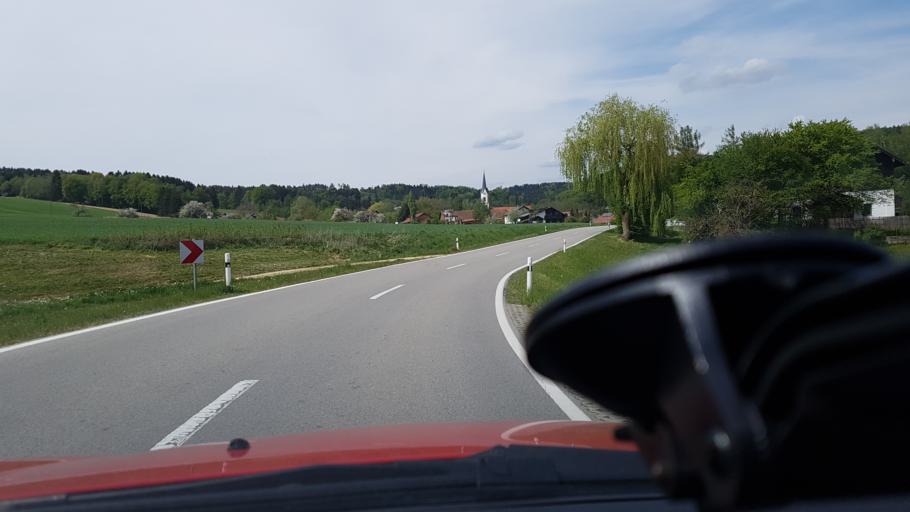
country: DE
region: Bavaria
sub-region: Lower Bavaria
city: Stubenberg
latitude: 48.3368
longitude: 13.0875
